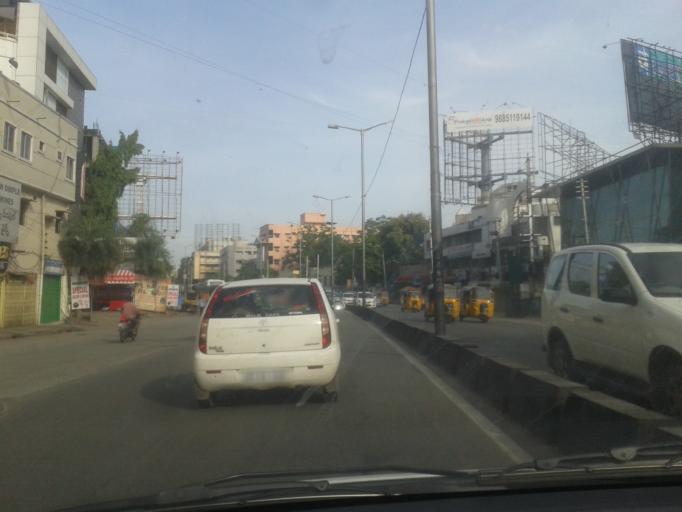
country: IN
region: Telangana
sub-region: Hyderabad
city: Hyderabad
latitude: 17.4034
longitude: 78.4571
